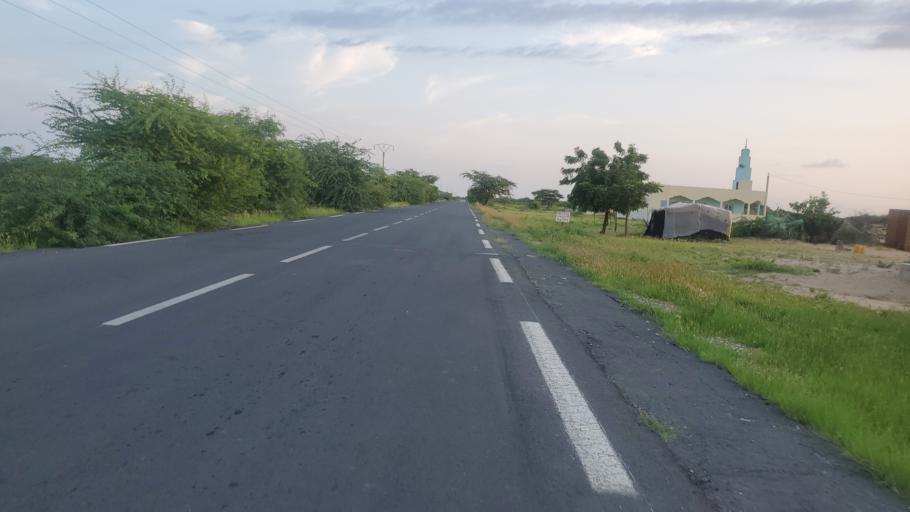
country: SN
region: Saint-Louis
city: Saint-Louis
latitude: 16.1325
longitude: -16.4122
